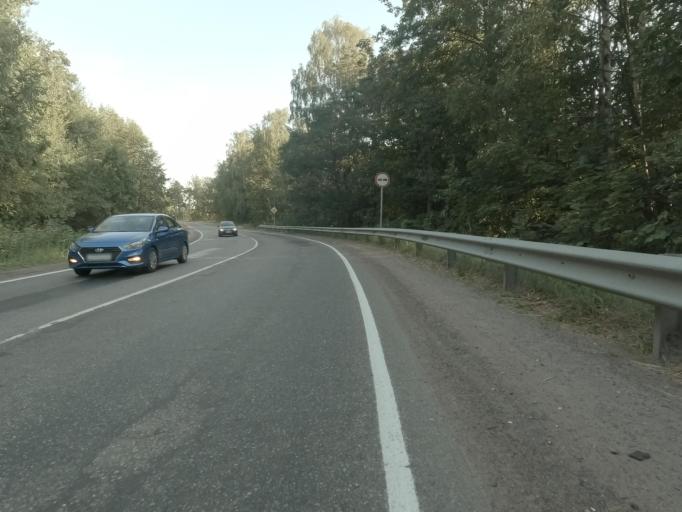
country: RU
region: Leningrad
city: Vyborg
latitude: 60.7282
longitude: 28.7595
